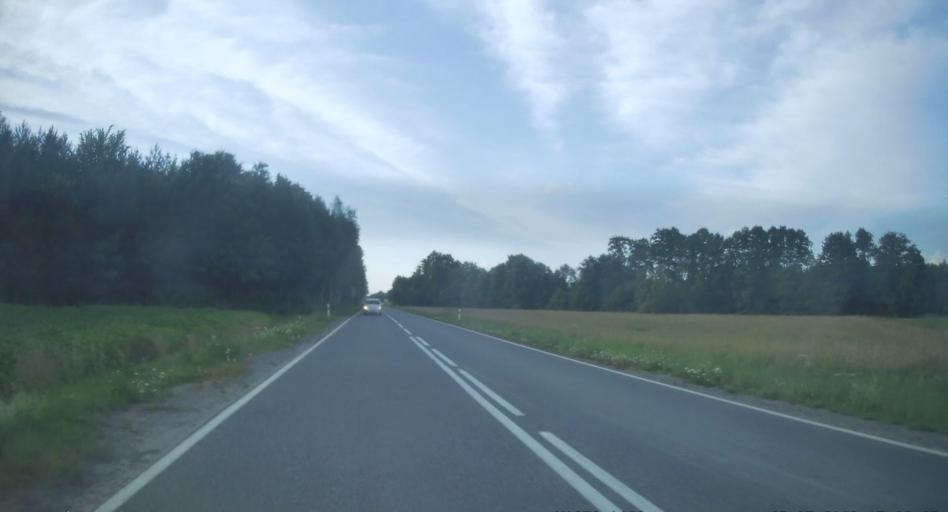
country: PL
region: Lesser Poland Voivodeship
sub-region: Powiat brzeski
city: Szczurowa
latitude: 50.0785
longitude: 20.6334
